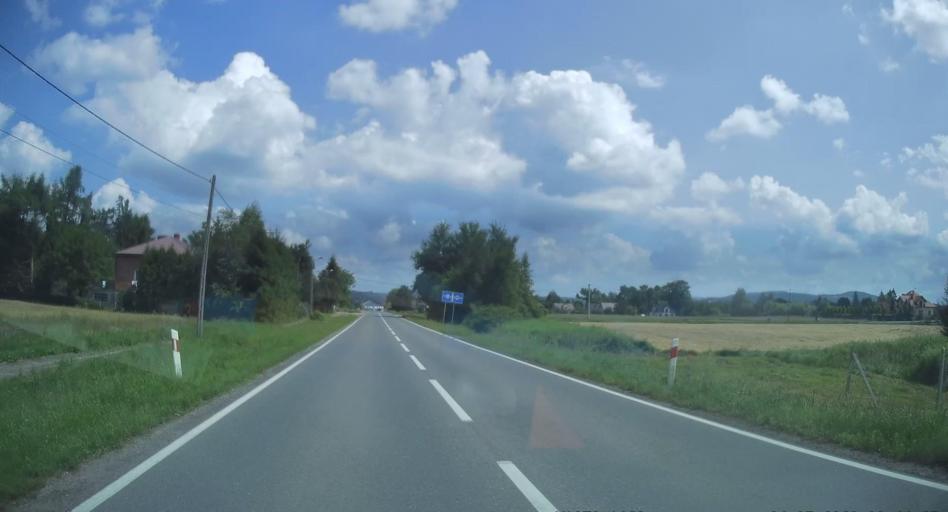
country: PL
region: Lesser Poland Voivodeship
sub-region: Powiat tarnowski
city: Zakliczyn
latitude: 49.8524
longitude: 20.8114
